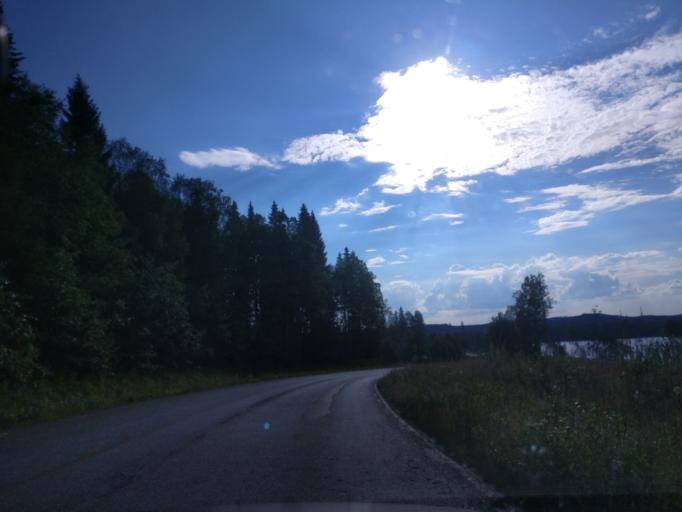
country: SE
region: Dalarna
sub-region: Ludvika Kommun
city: Ludvika
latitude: 60.2891
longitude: 15.1799
